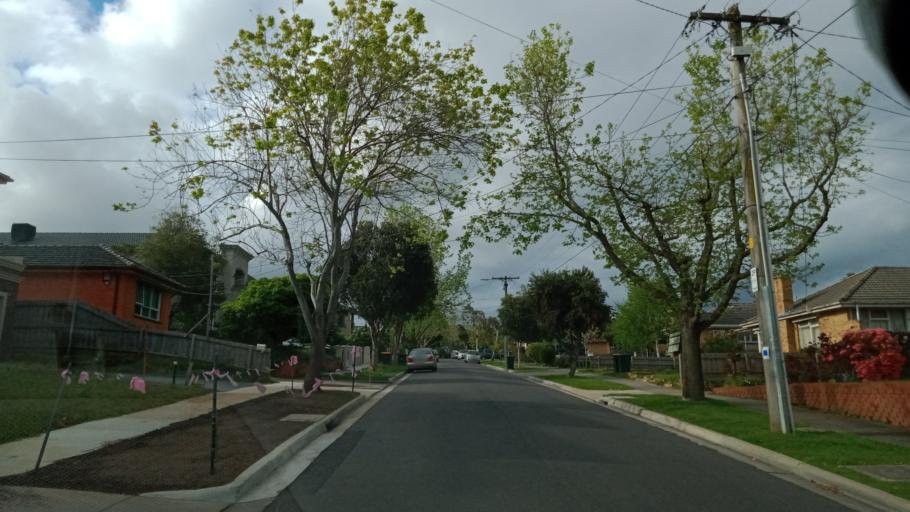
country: AU
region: Victoria
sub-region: Monash
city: Notting Hill
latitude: -37.8802
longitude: 145.1553
